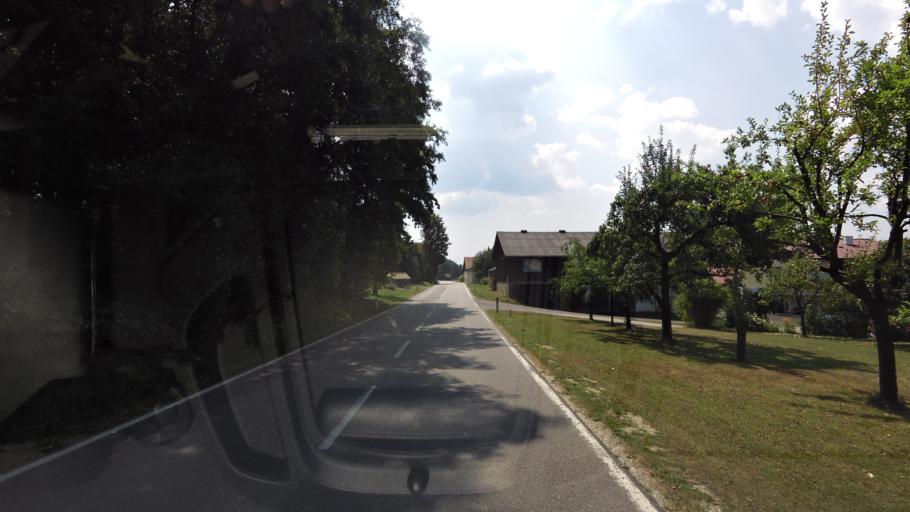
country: AT
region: Upper Austria
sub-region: Politischer Bezirk Ried im Innkreis
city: Waldzell
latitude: 48.1623
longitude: 13.4238
